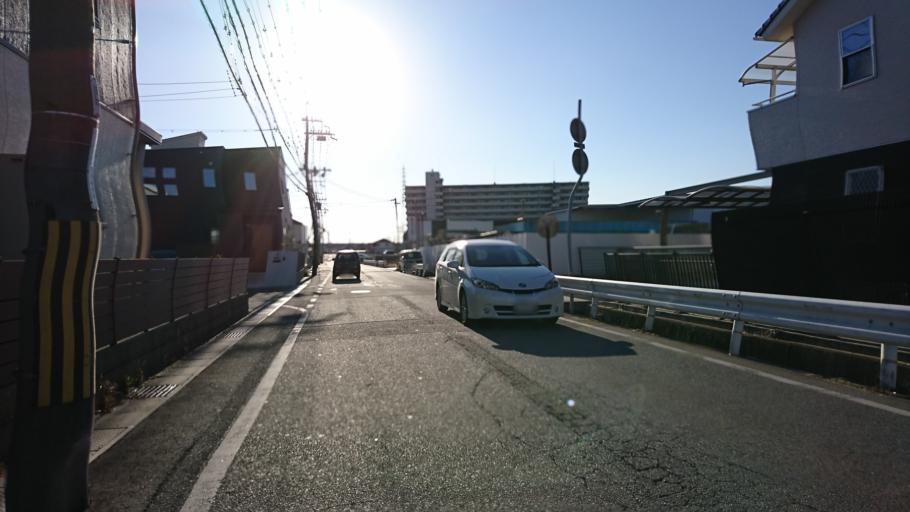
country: JP
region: Hyogo
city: Kakogawacho-honmachi
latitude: 34.7444
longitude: 134.8375
